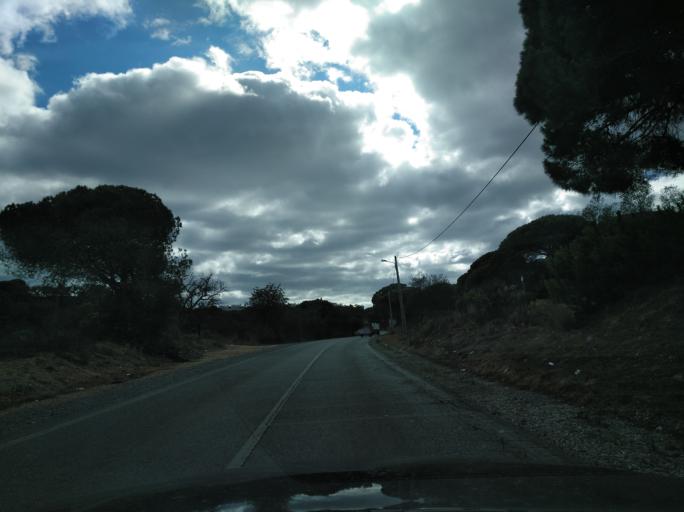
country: PT
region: Faro
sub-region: Vila Real de Santo Antonio
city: Monte Gordo
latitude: 37.1871
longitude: -7.4844
